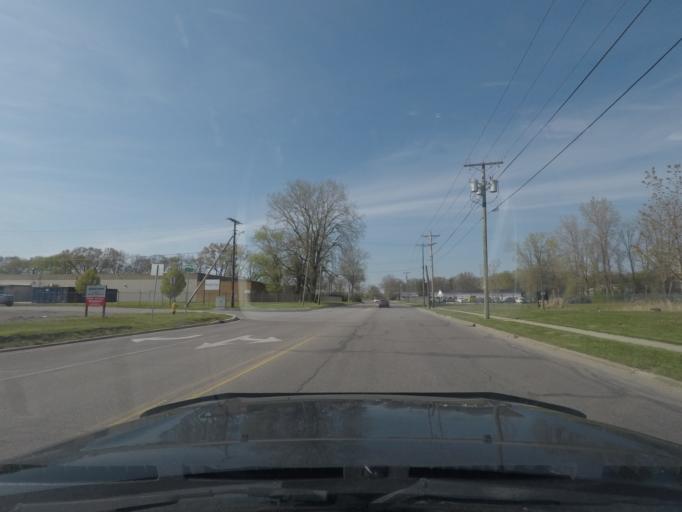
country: US
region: Indiana
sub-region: Elkhart County
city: Elkhart
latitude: 41.7014
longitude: -86.0036
